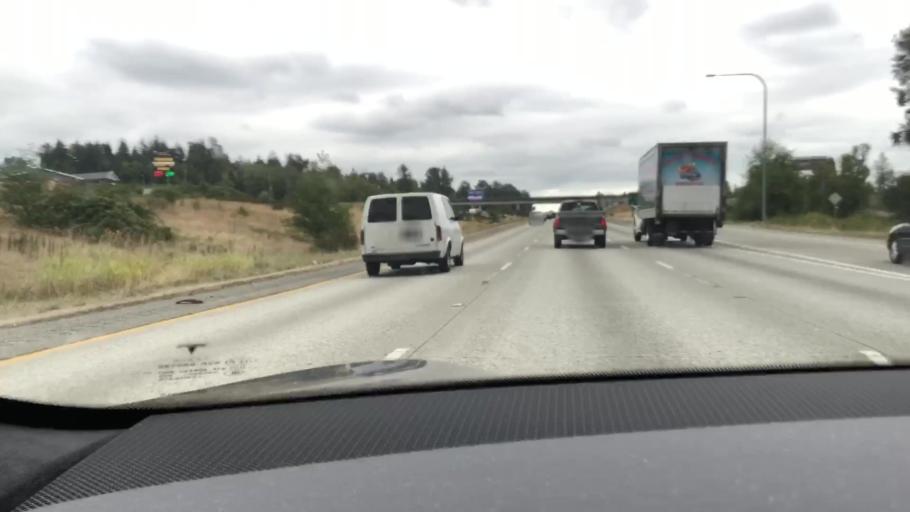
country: US
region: Washington
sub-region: Snohomish County
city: Smokey Point
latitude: 48.2084
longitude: -122.2178
